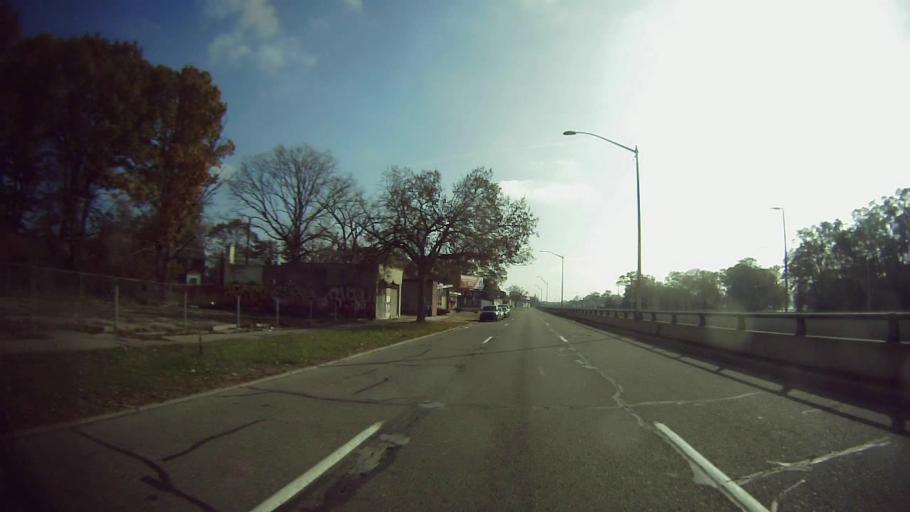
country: US
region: Michigan
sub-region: Oakland County
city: Oak Park
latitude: 42.4126
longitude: -83.1678
